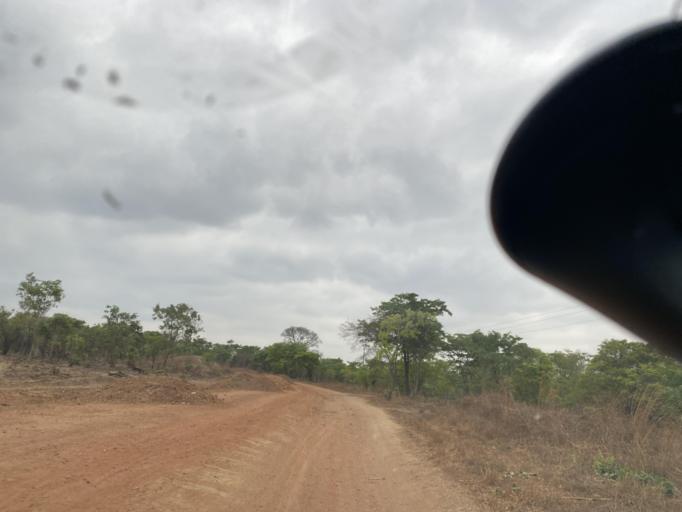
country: ZM
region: Lusaka
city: Chongwe
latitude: -15.2268
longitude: 28.7331
